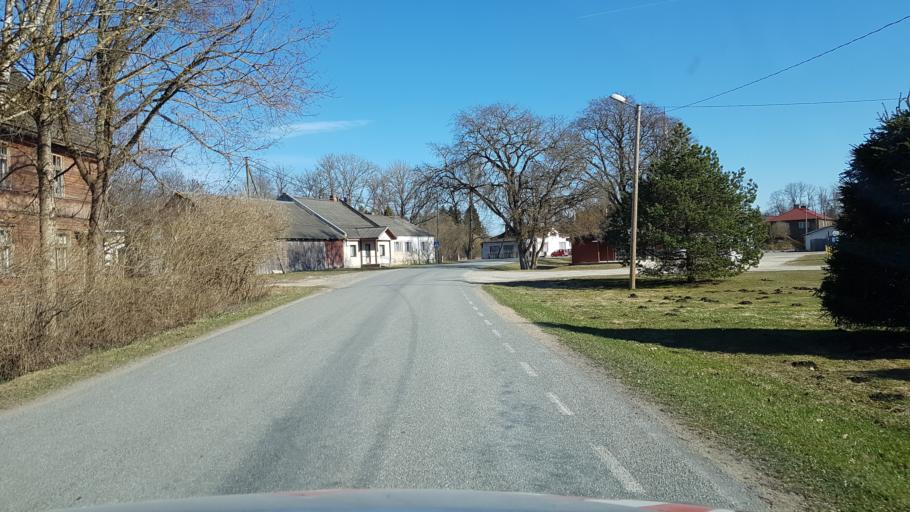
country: EE
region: Laeaene-Virumaa
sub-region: Rakke vald
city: Rakke
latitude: 59.0461
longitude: 26.3992
